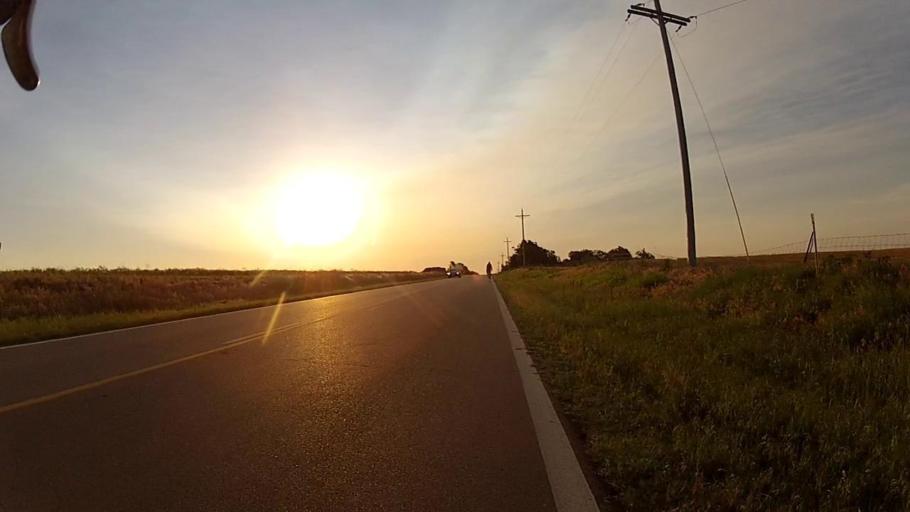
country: US
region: Kansas
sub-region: Harper County
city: Anthony
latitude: 37.1526
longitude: -97.9566
